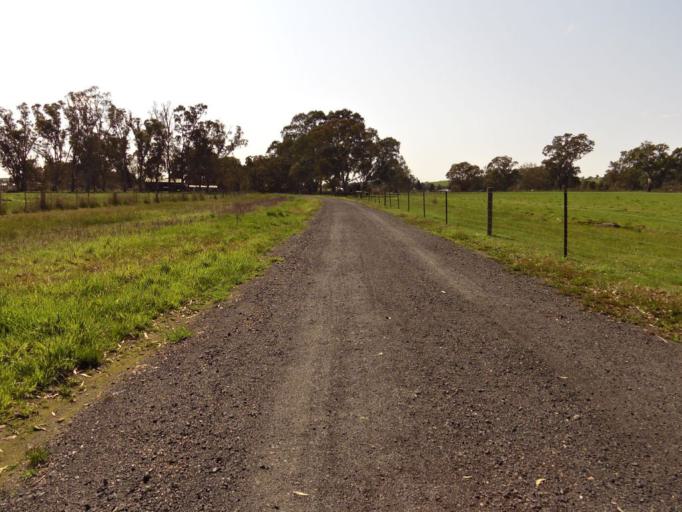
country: AU
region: Victoria
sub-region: Murrindindi
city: Alexandra
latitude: -37.1103
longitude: 145.6118
